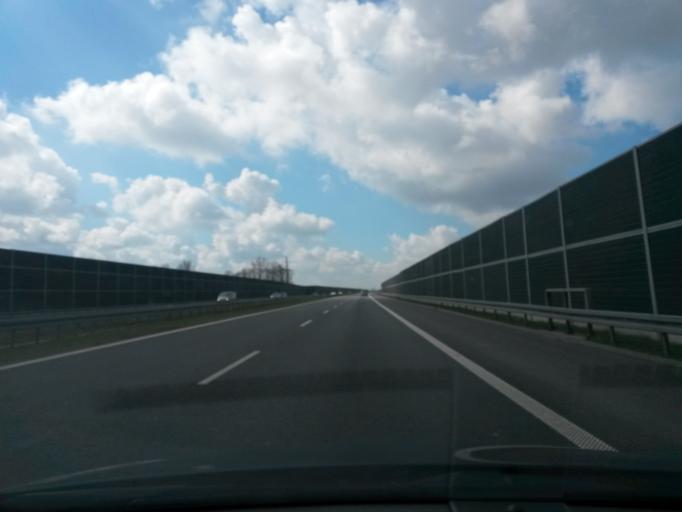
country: PL
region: Masovian Voivodeship
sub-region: Powiat zyrardowski
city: Wiskitki
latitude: 52.1020
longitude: 20.4274
